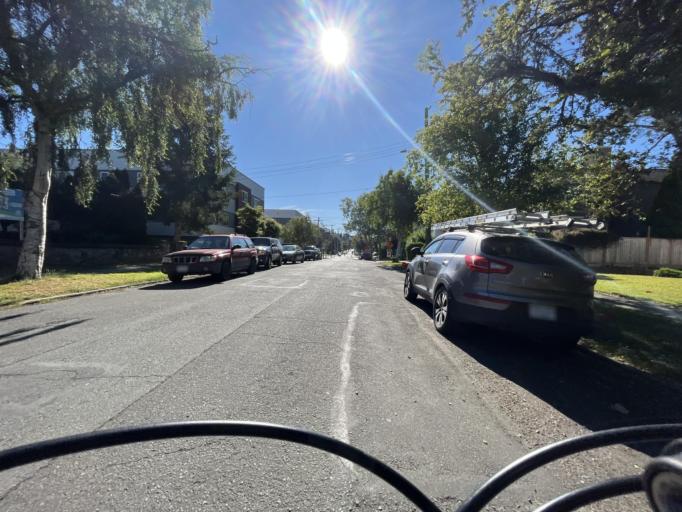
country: CA
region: British Columbia
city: Victoria
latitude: 48.4197
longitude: -123.3562
